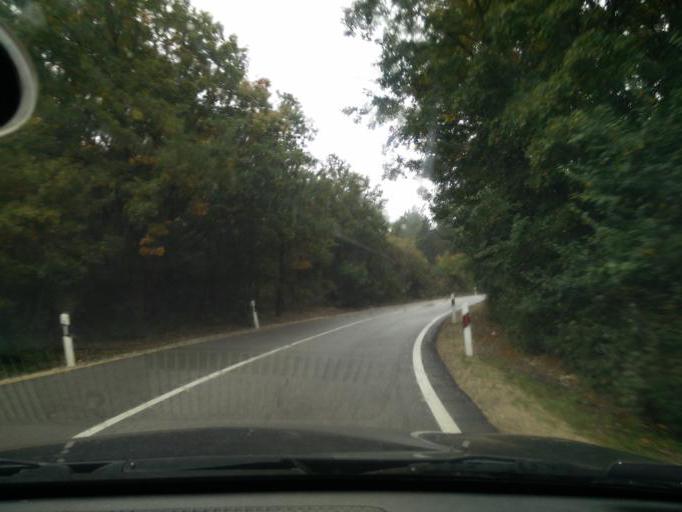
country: HU
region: Komarom-Esztergom
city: Tarjan
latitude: 47.6359
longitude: 18.5487
